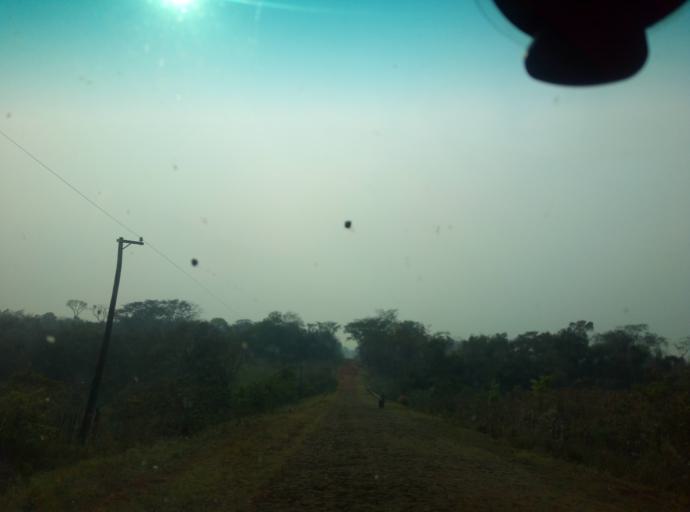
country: PY
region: Caaguazu
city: Carayao
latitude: -25.2040
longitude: -56.2424
